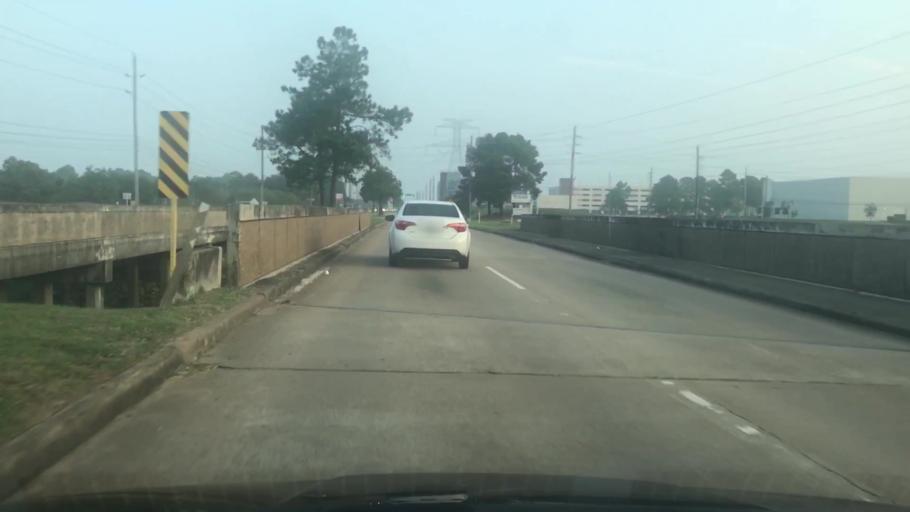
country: US
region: Texas
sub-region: Fort Bend County
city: Cinco Ranch
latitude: 29.7910
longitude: -95.7518
